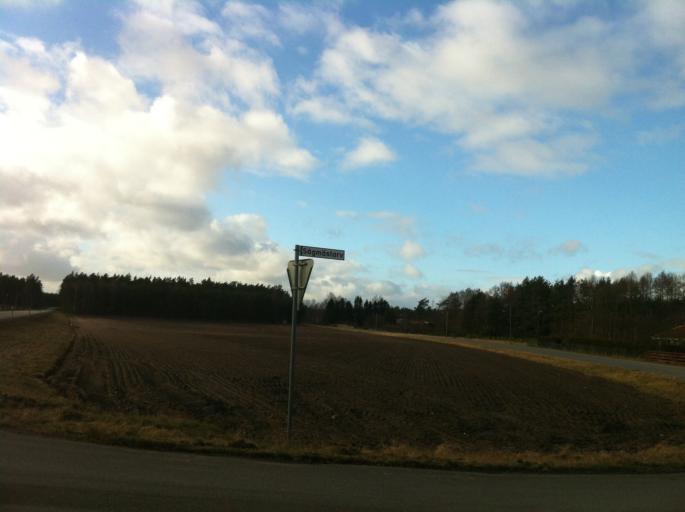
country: SE
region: Skane
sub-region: Bromolla Kommun
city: Bromoella
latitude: 56.0631
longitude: 14.5150
